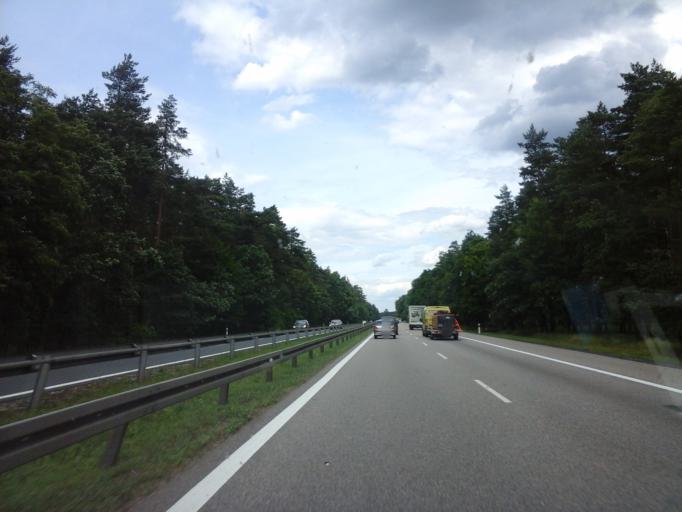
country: PL
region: West Pomeranian Voivodeship
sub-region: Powiat goleniowski
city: Goleniow
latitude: 53.4419
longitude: 14.7800
